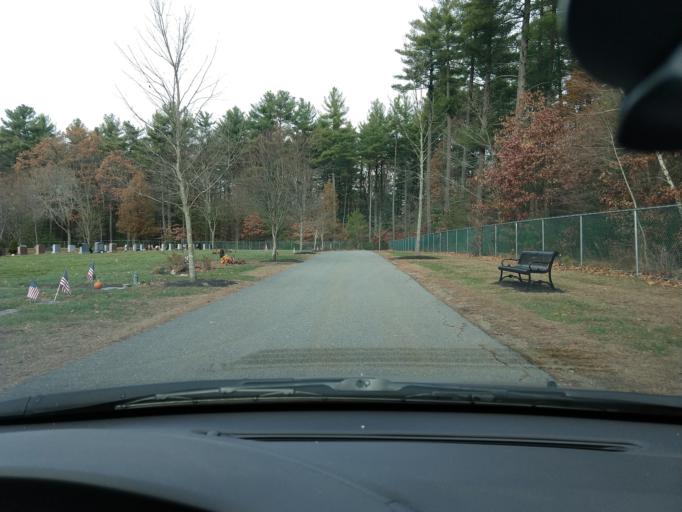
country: US
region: Massachusetts
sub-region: Middlesex County
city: Bedford
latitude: 42.4866
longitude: -71.2523
